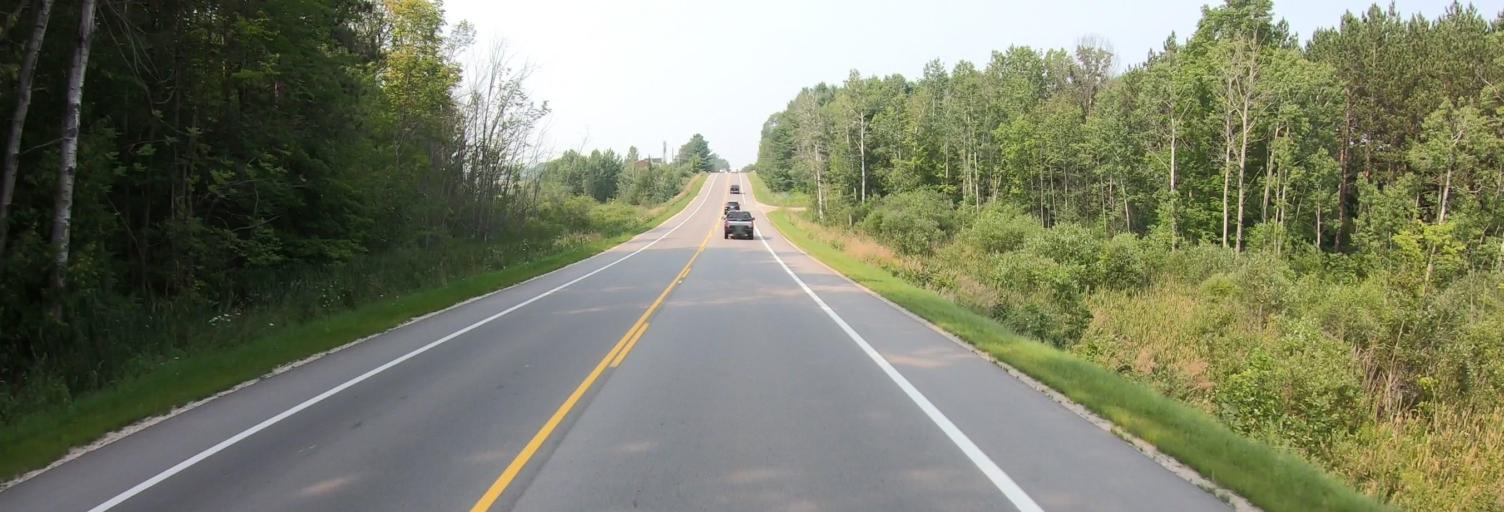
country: US
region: Michigan
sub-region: Charlevoix County
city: Charlevoix
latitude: 45.2272
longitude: -85.2613
